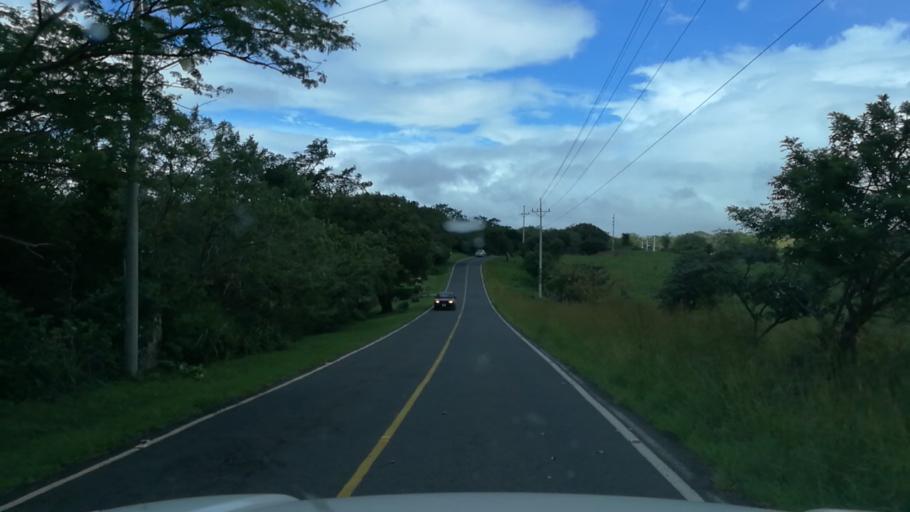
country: CR
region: Guanacaste
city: Fortuna
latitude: 10.6441
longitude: -85.2314
